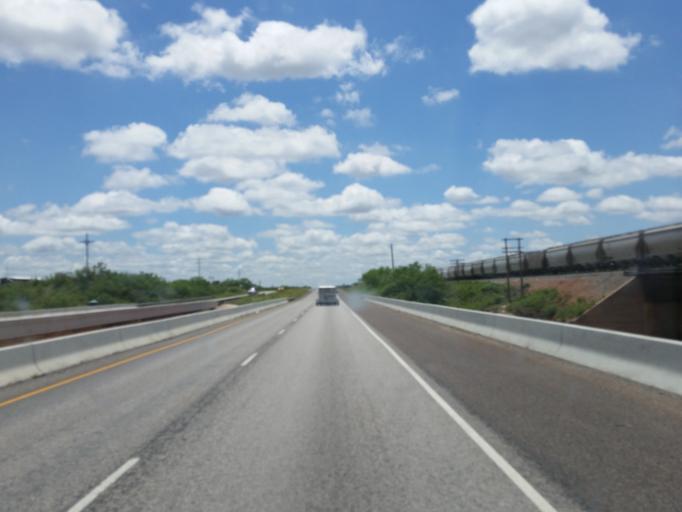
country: US
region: Texas
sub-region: Garza County
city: Post
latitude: 33.0389
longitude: -101.1993
